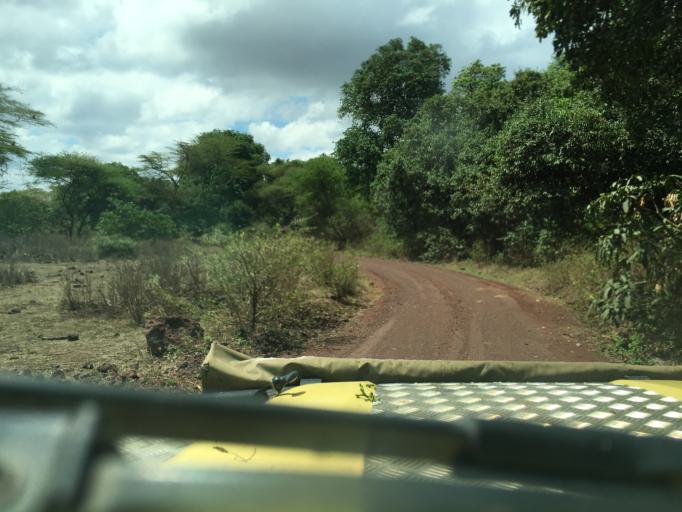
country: TZ
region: Arusha
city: Mto wa Mbu
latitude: -3.4168
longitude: 35.8194
